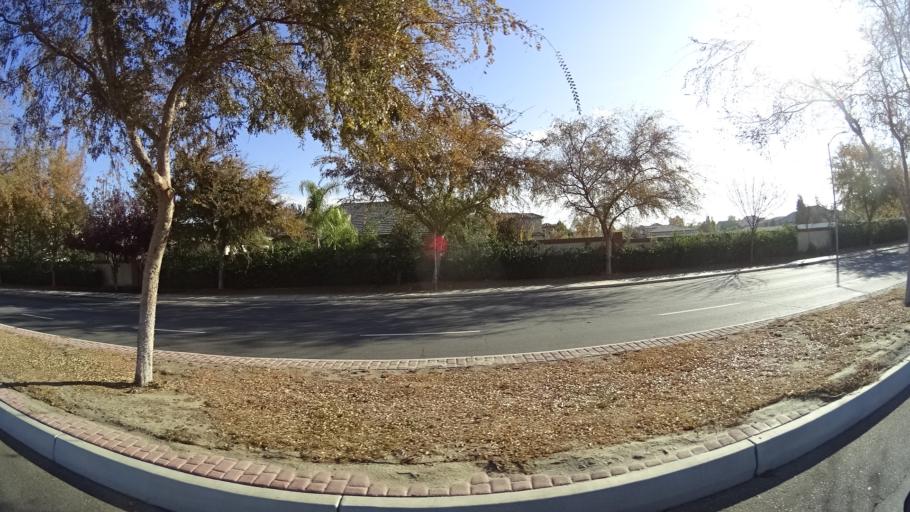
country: US
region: California
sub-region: Kern County
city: Rosedale
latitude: 35.3354
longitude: -119.1457
